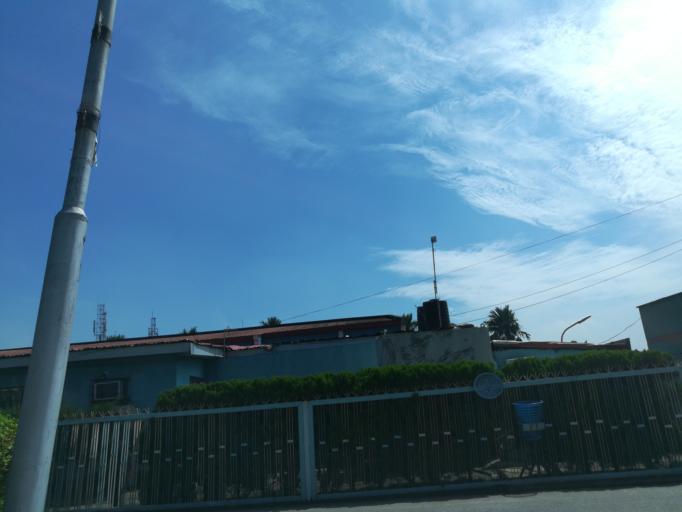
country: NG
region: Lagos
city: Ikeja
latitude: 6.6059
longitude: 3.3466
